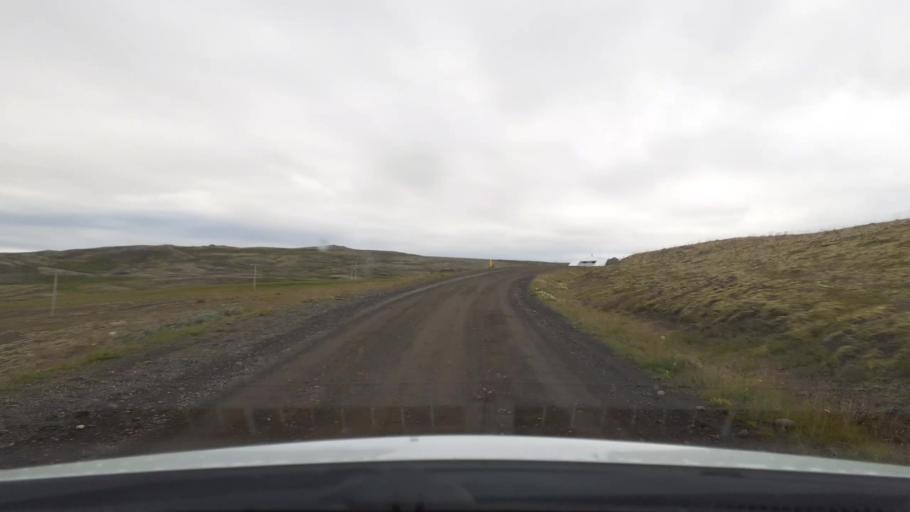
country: IS
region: Capital Region
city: Mosfellsbaer
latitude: 64.2063
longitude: -21.5645
